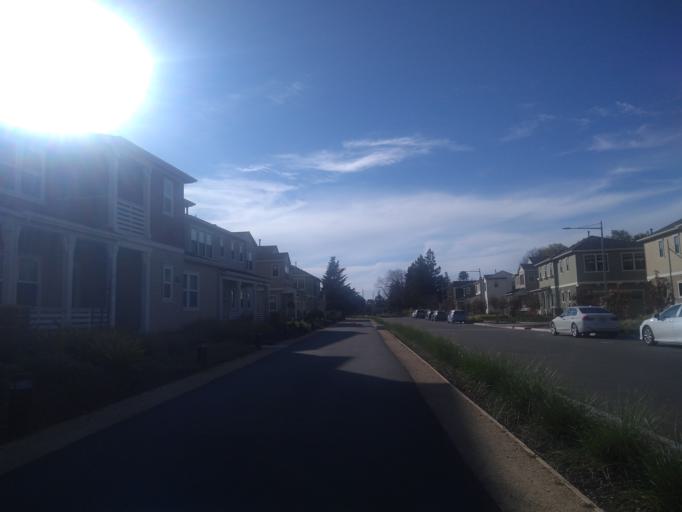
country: US
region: California
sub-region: Santa Clara County
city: Mountain View
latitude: 37.4009
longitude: -122.0607
